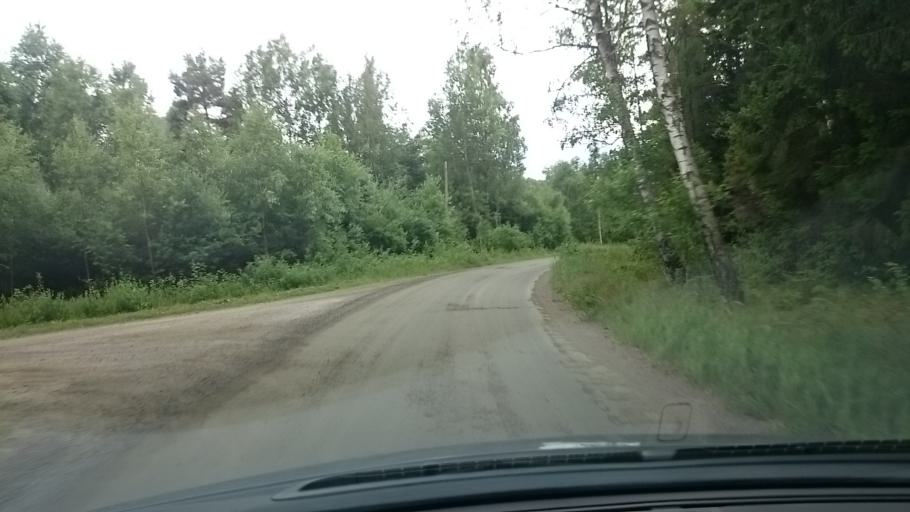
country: SE
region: Vaestra Goetaland
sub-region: Karlsborgs Kommun
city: Karlsborg
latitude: 58.6880
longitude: 14.6132
